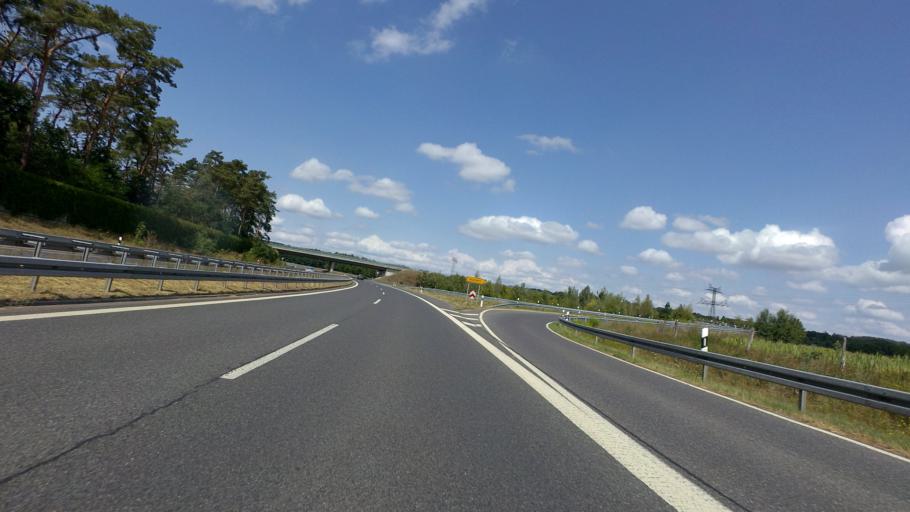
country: DE
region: Brandenburg
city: Rangsdorf
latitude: 52.3485
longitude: 13.4448
